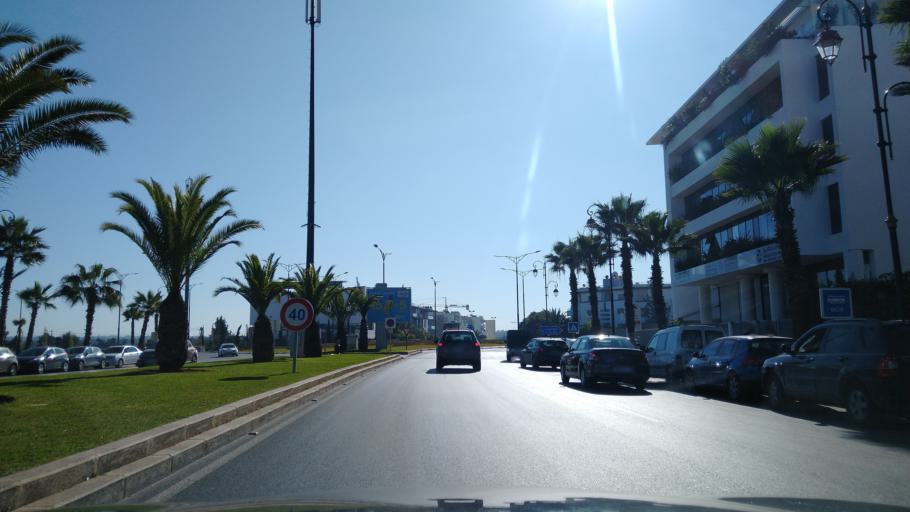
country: MA
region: Rabat-Sale-Zemmour-Zaer
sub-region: Skhirate-Temara
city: Temara
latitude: 33.9504
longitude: -6.8606
